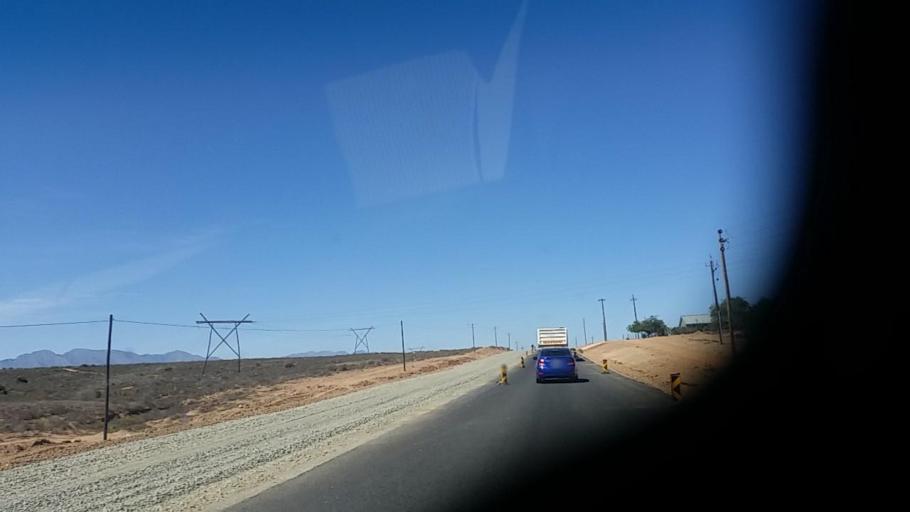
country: ZA
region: Western Cape
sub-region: Eden District Municipality
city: Oudtshoorn
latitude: -33.5919
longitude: 22.2382
